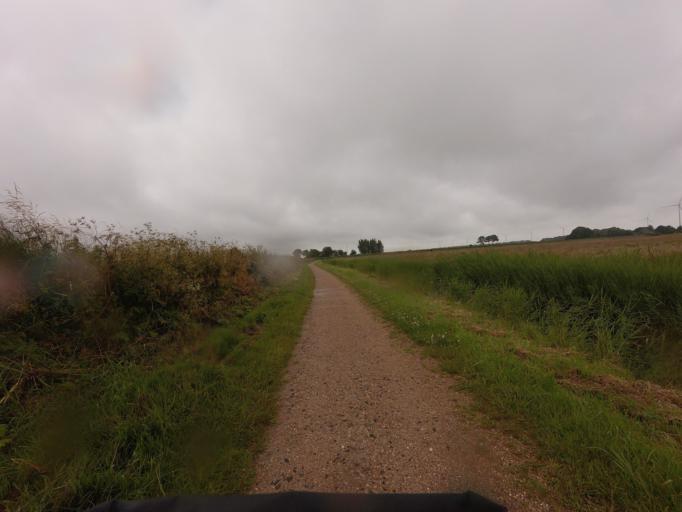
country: NL
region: North Holland
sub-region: Gemeente Opmeer
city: Opmeer
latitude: 52.7484
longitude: 4.9423
